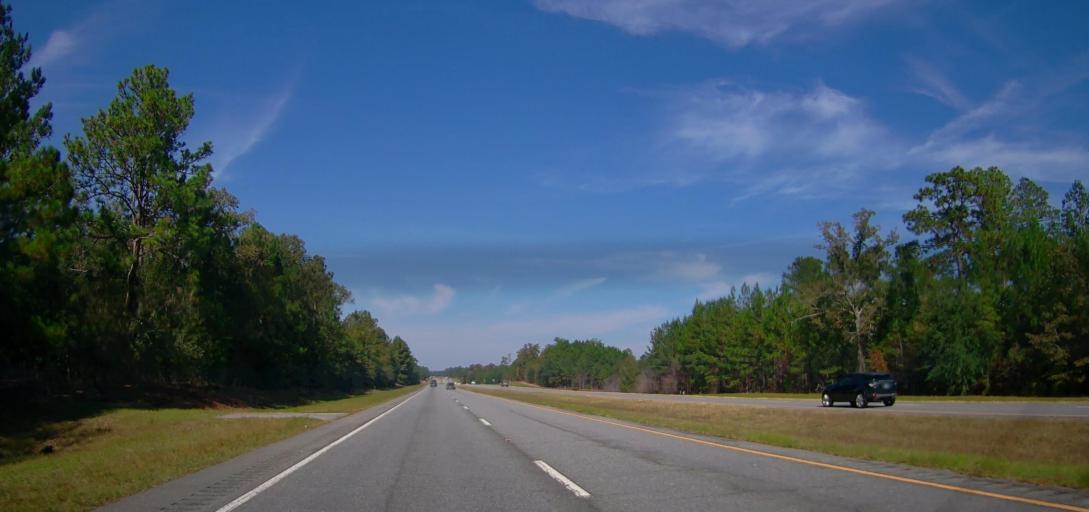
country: US
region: Georgia
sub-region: Lee County
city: Leesburg
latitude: 31.7115
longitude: -83.9897
